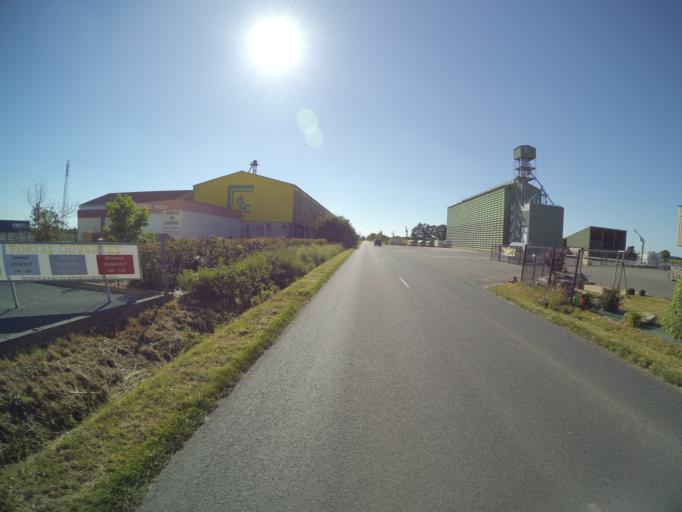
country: FR
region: Pays de la Loire
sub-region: Departement de la Vendee
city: La Boissiere-de-Montaigu
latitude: 46.9497
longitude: -1.2019
